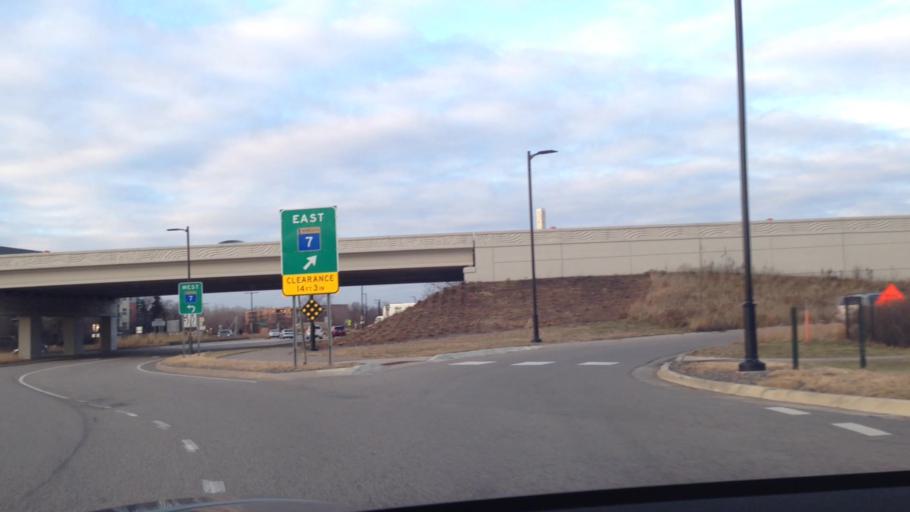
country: US
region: Minnesota
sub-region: Hennepin County
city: Saint Louis Park
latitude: 44.9372
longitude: -93.3689
